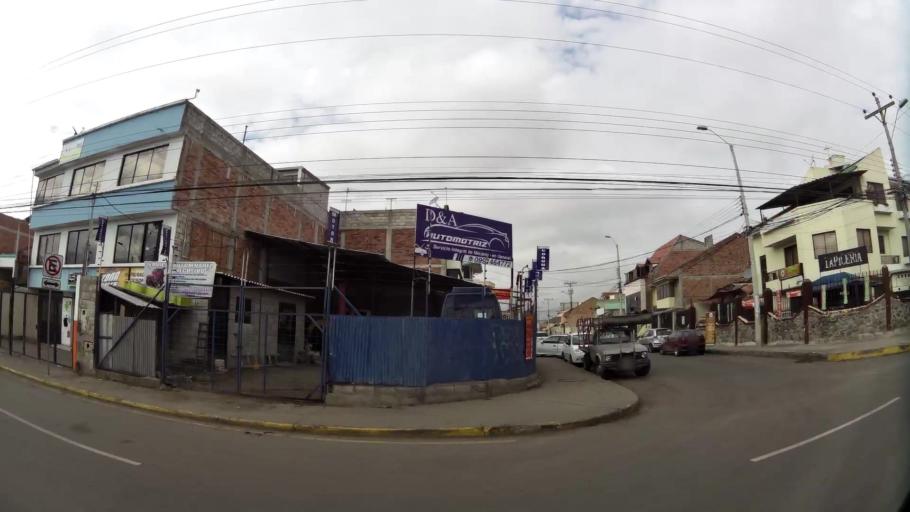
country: EC
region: Azuay
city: Cuenca
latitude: -2.8881
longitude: -78.9785
